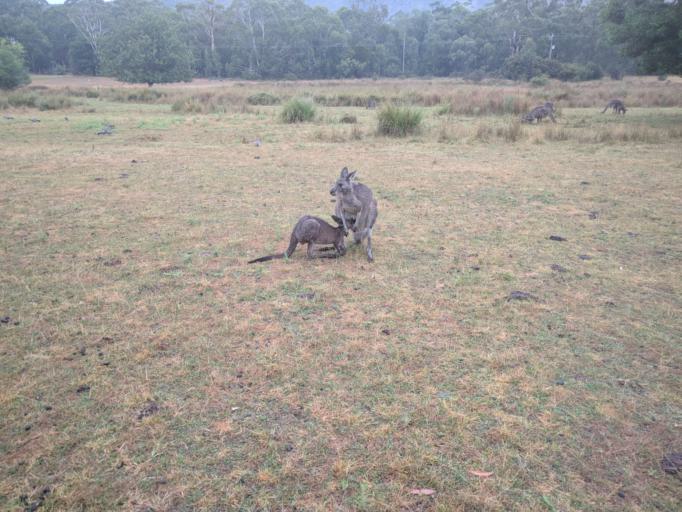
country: AU
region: Victoria
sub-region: Northern Grampians
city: Stawell
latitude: -37.1702
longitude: 142.5421
